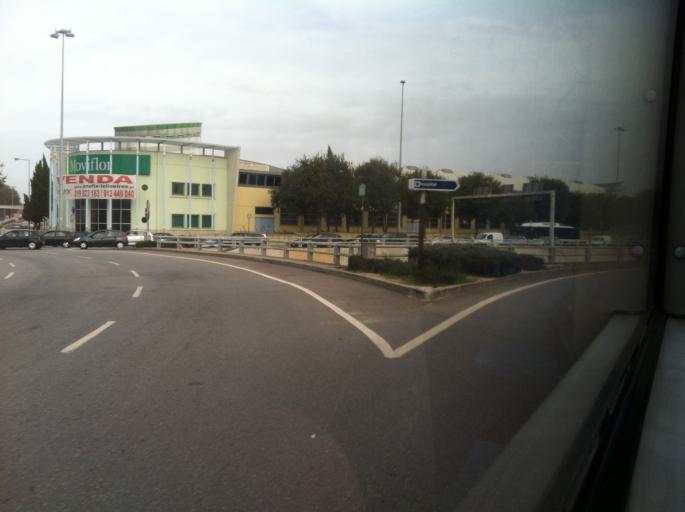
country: PT
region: Porto
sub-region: Matosinhos
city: Senhora da Hora
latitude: 41.1777
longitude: -8.6556
